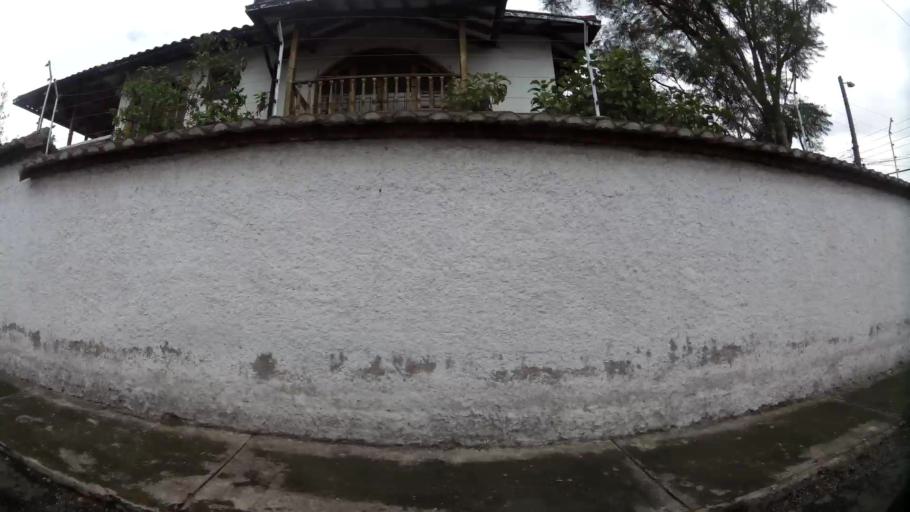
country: EC
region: Pichincha
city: Sangolqui
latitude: -0.3056
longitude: -78.4653
